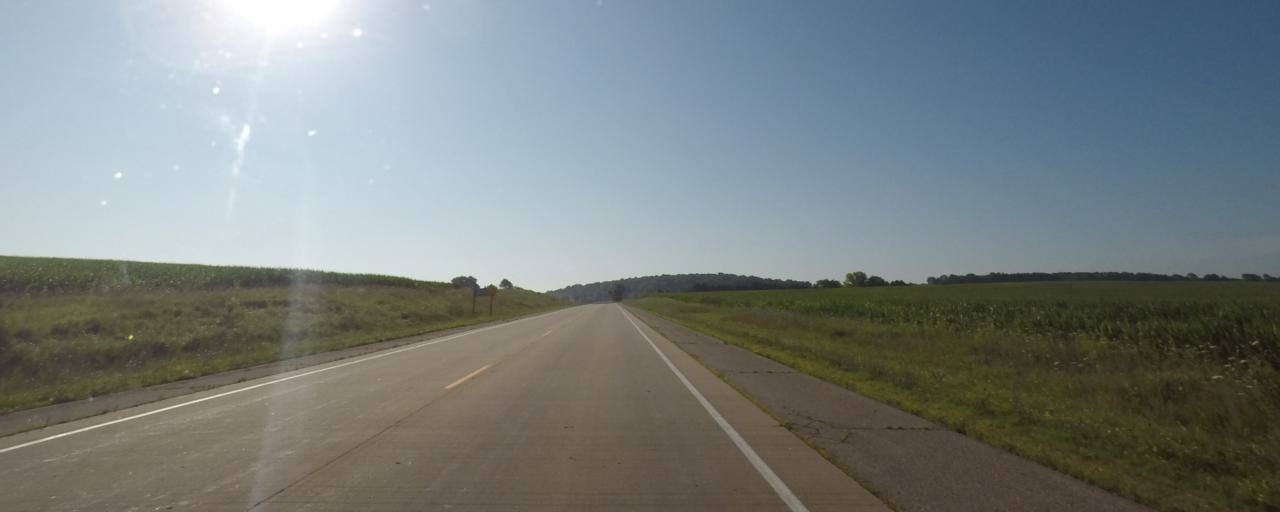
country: US
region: Wisconsin
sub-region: Jefferson County
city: Lake Ripley
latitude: 42.9756
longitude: -88.9518
